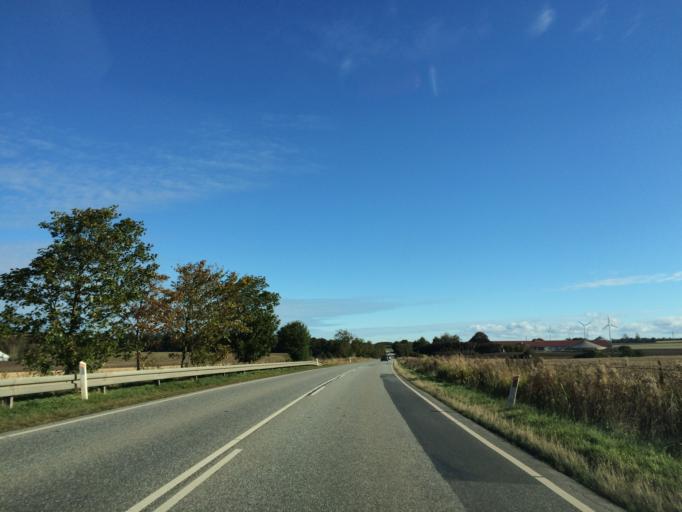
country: DK
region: Central Jutland
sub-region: Randers Kommune
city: Langa
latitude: 56.3940
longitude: 9.9749
